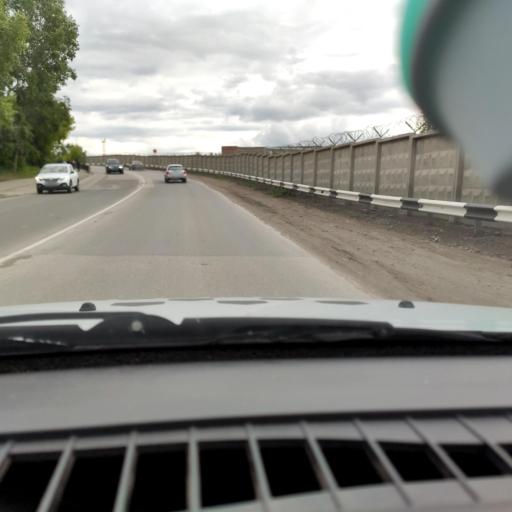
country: RU
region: Perm
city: Chusovoy
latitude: 58.2898
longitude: 57.8141
